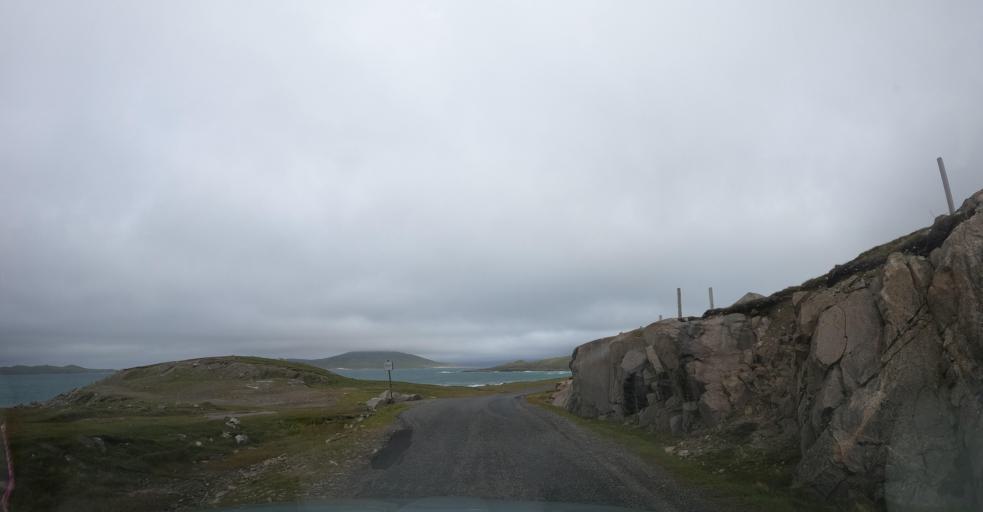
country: GB
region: Scotland
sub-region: Eilean Siar
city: Harris
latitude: 57.8563
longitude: -6.9984
